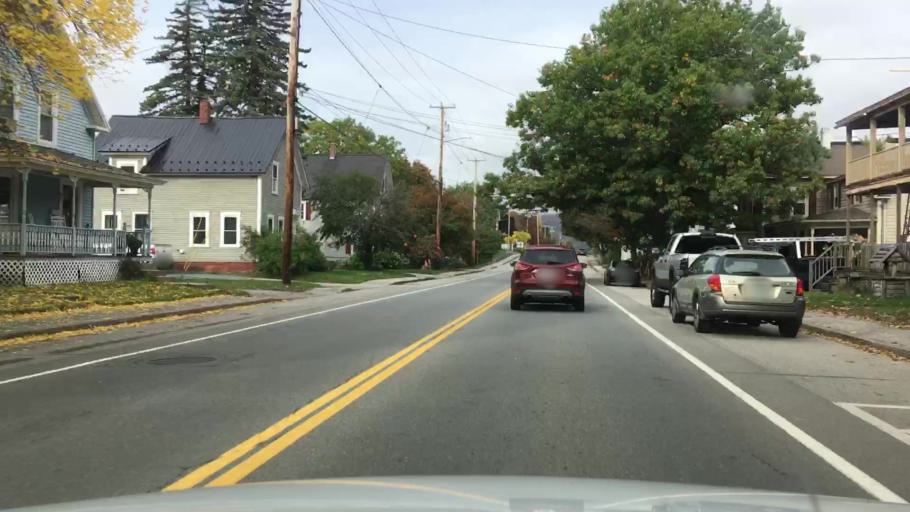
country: US
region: New Hampshire
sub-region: Coos County
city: Gorham
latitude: 44.3873
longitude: -71.1697
